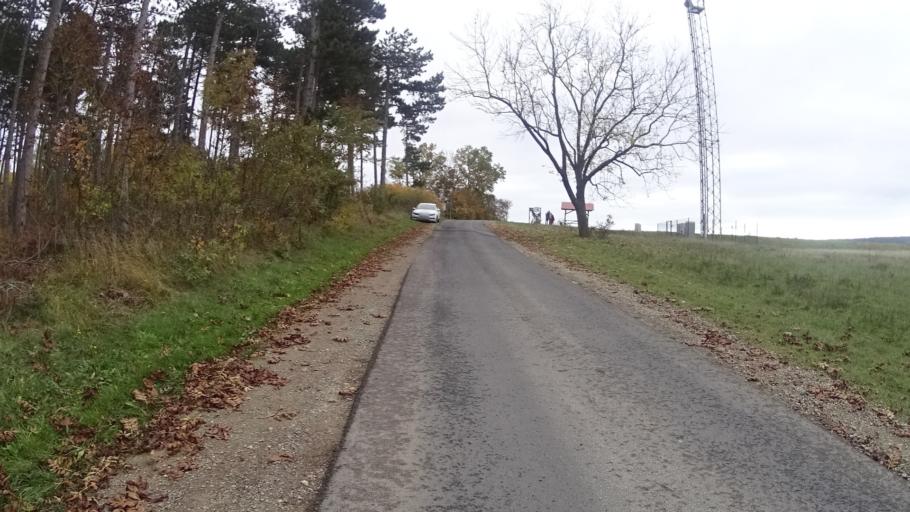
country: DE
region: Thuringia
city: Gossel
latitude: 50.8419
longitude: 10.8827
